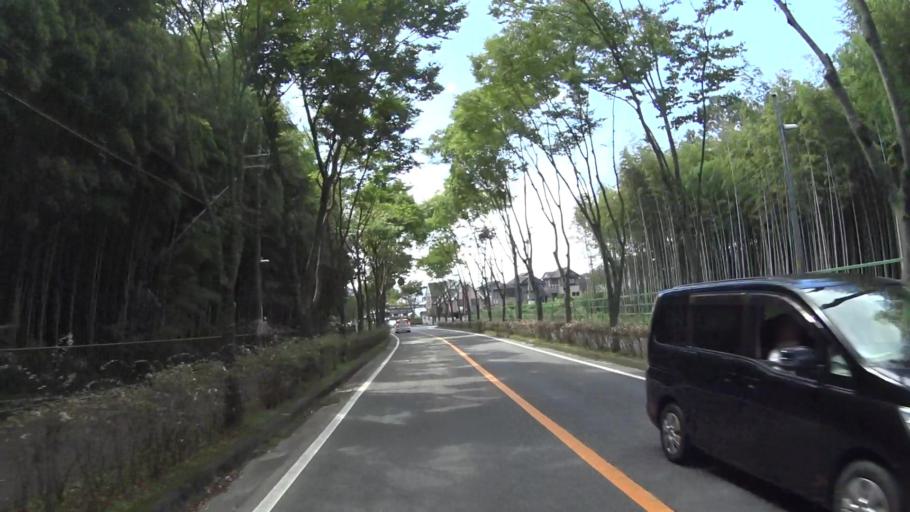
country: JP
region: Kyoto
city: Uji
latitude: 34.8540
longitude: 135.7970
